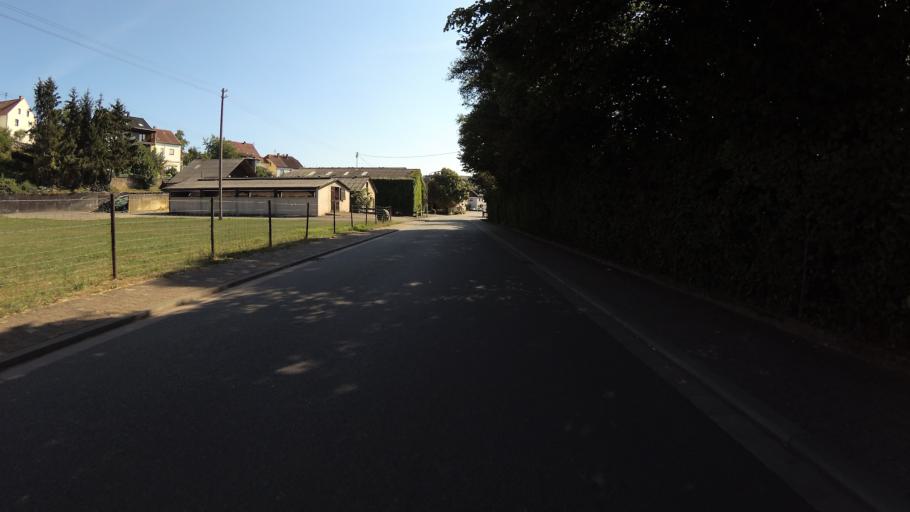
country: DE
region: Saarland
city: Eppelborn
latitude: 49.4147
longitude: 6.9518
